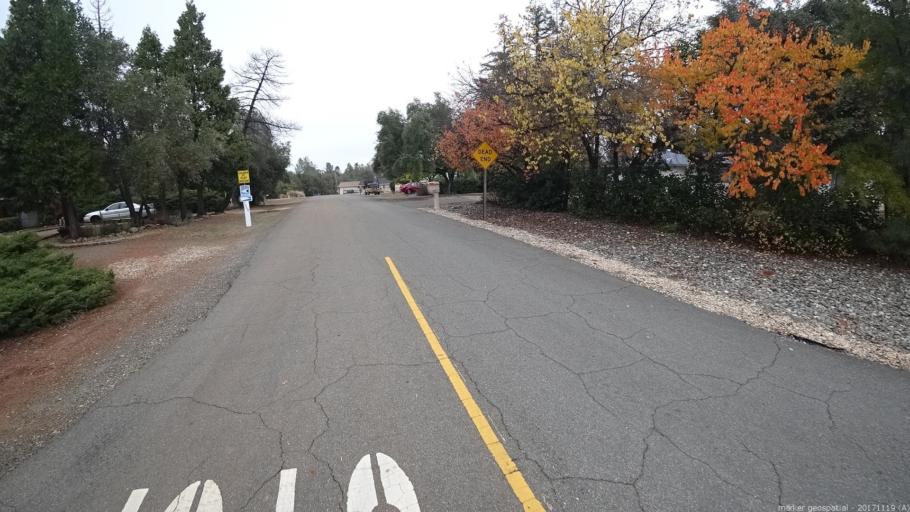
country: US
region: California
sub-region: Shasta County
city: Redding
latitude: 40.4893
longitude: -122.4121
